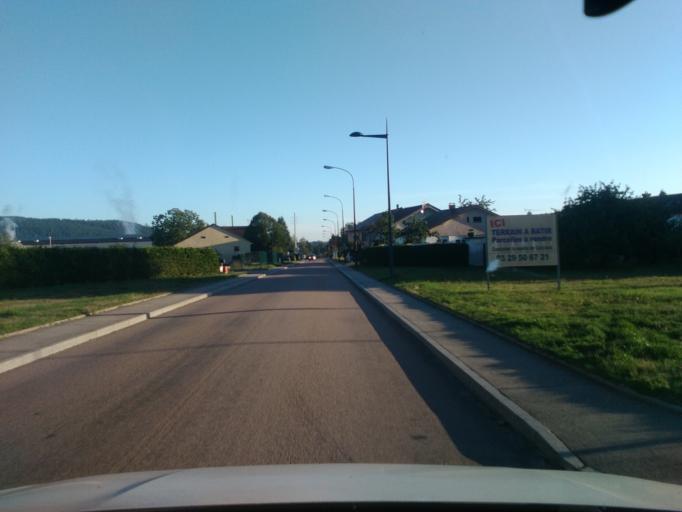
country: FR
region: Lorraine
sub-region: Departement des Vosges
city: Corcieux
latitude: 48.1763
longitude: 6.8834
